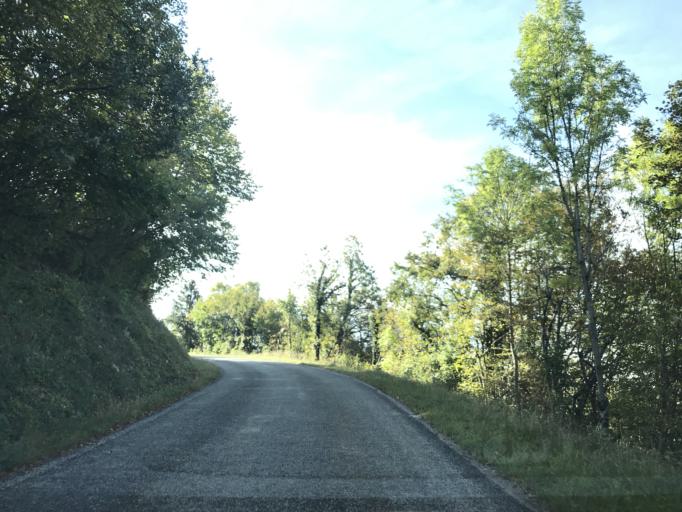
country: FR
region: Rhone-Alpes
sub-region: Departement de la Savoie
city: Novalaise
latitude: 45.6416
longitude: 5.7961
